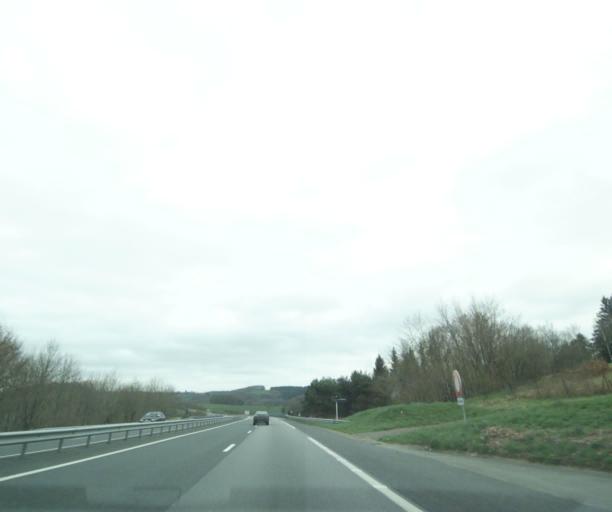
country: FR
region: Limousin
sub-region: Departement de la Correze
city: Vigeois
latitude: 45.4130
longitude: 1.5240
